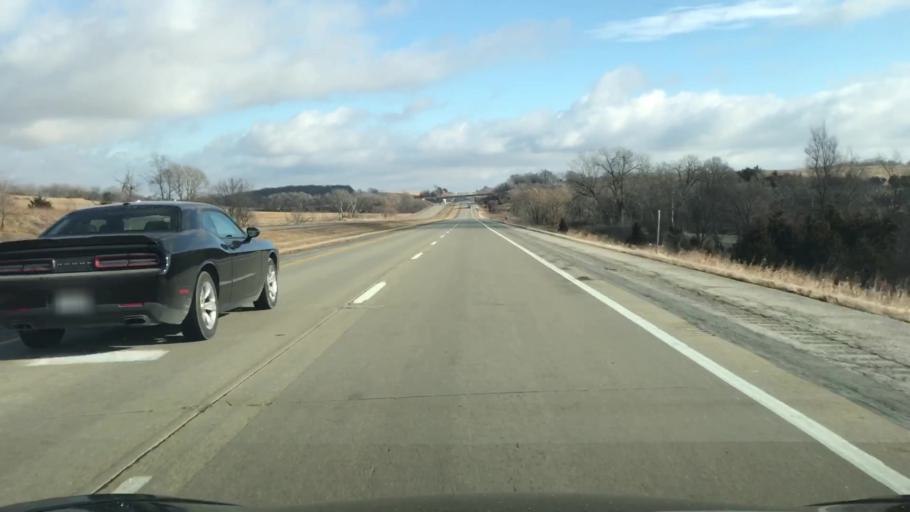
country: US
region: Iowa
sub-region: Cass County
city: Atlantic
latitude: 41.4970
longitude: -94.8451
